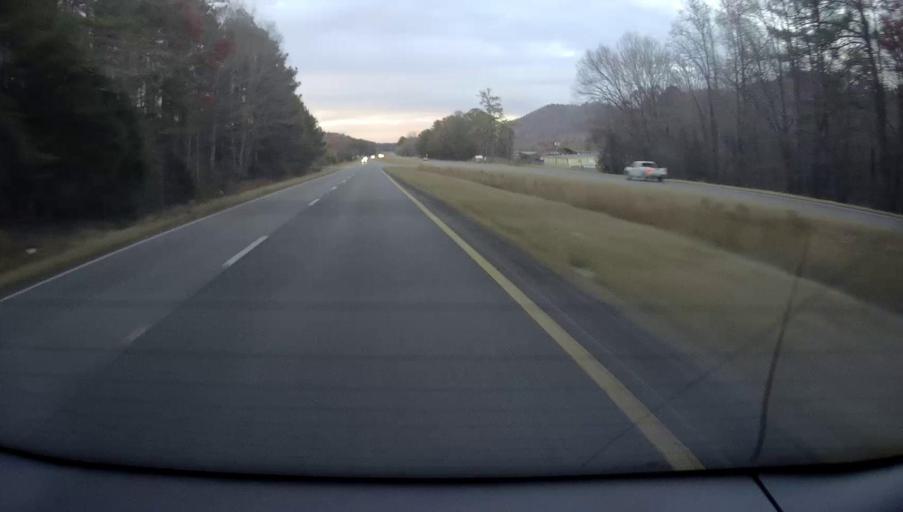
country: US
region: Alabama
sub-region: Etowah County
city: Glencoe
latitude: 33.9200
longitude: -85.9137
